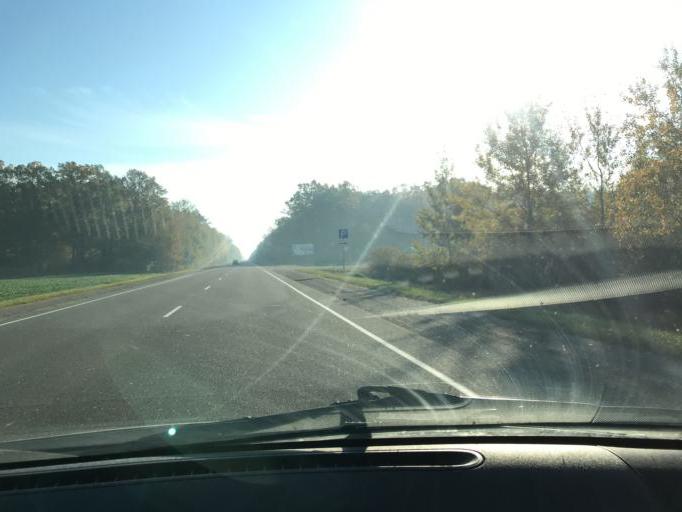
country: BY
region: Brest
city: Horad Luninyets
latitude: 52.3105
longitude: 26.6707
